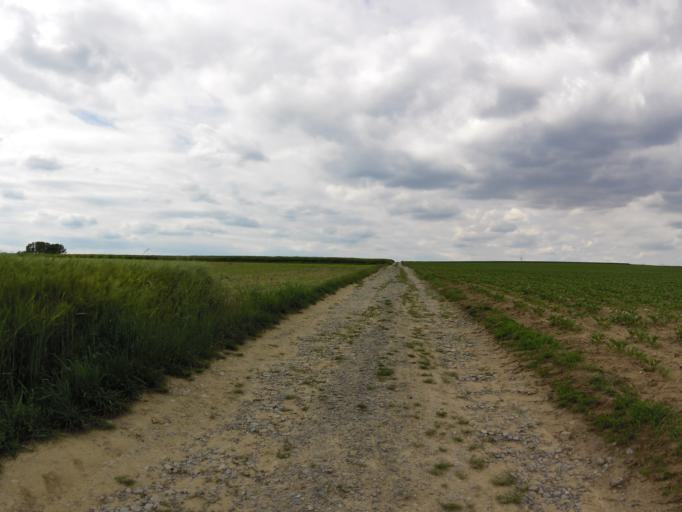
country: DE
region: Bavaria
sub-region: Regierungsbezirk Unterfranken
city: Theilheim
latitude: 49.7265
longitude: 10.0407
